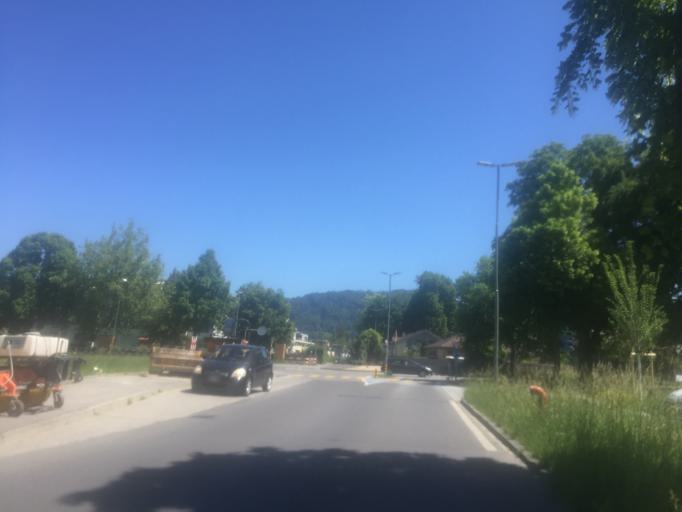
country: CH
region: Bern
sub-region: Thun District
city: Thun
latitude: 46.7479
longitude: 7.6103
